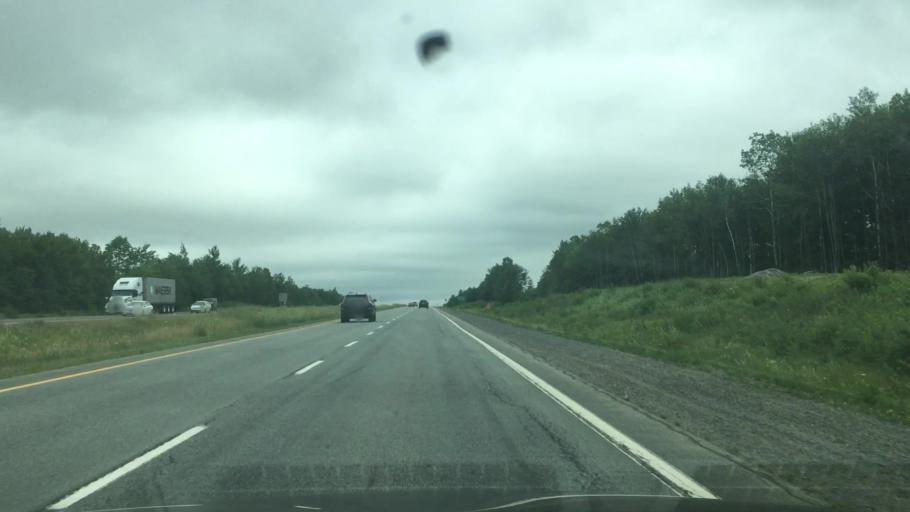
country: CA
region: Nova Scotia
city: Cole Harbour
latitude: 44.9859
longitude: -63.5007
